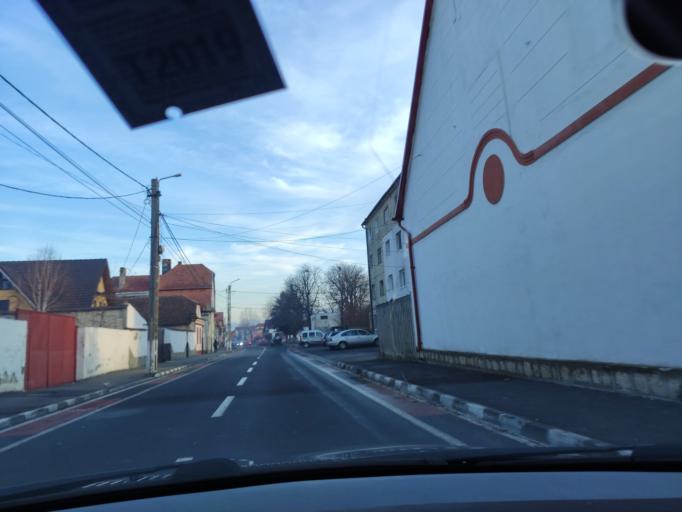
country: RO
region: Brasov
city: Codlea
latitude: 45.6970
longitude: 25.4495
